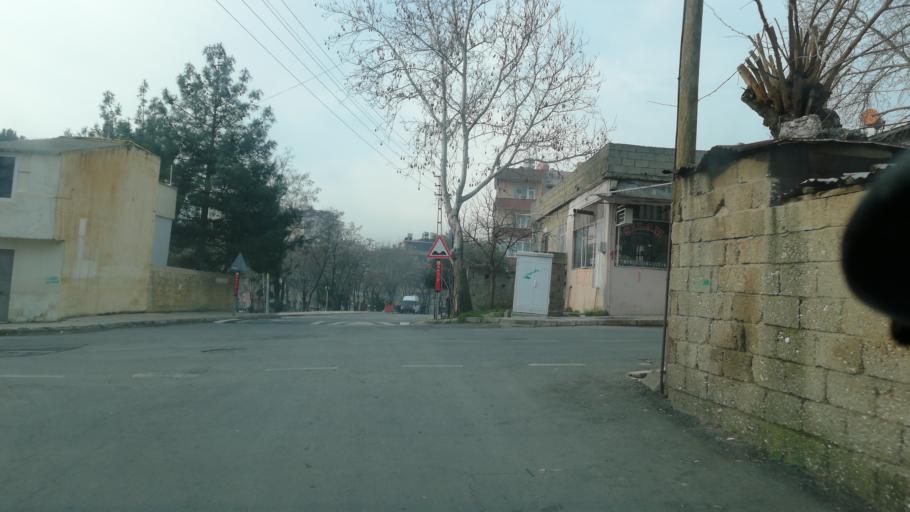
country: TR
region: Kahramanmaras
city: Kahramanmaras
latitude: 37.5904
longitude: 36.9080
